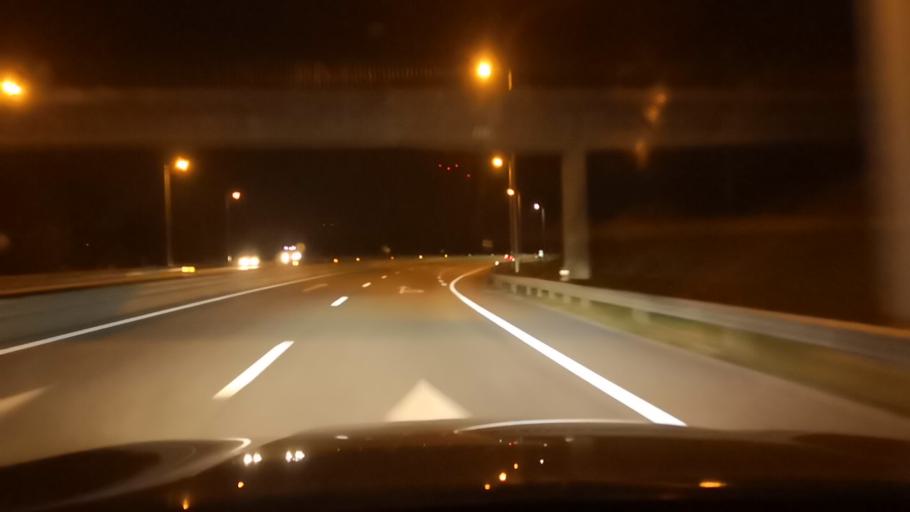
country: PT
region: Setubal
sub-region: Palmela
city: Palmela
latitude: 38.5735
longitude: -8.8667
